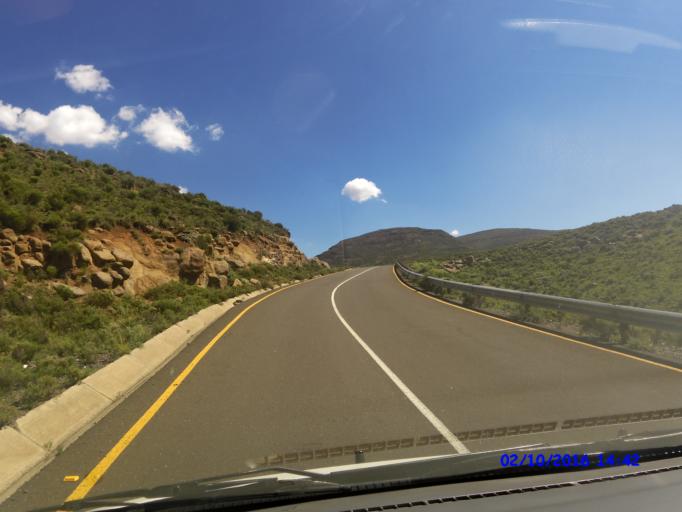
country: LS
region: Maseru
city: Nako
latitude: -29.5283
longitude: 28.0599
